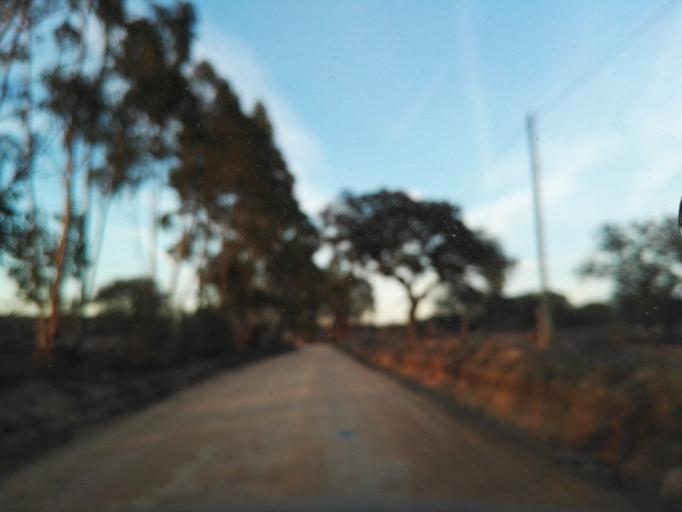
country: PT
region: Evora
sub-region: Montemor-O-Novo
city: Montemor-o-Novo
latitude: 38.7788
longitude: -8.2275
